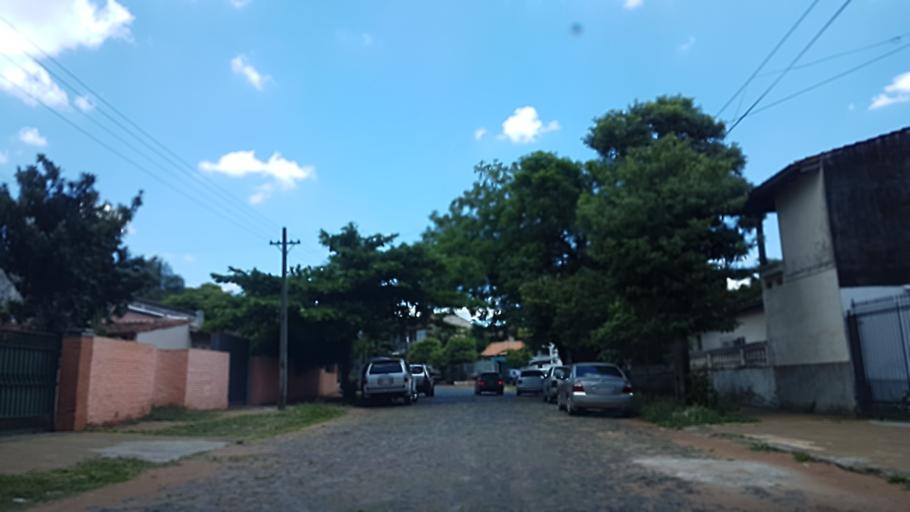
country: PY
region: Central
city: Lambare
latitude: -25.3187
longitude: -57.5722
